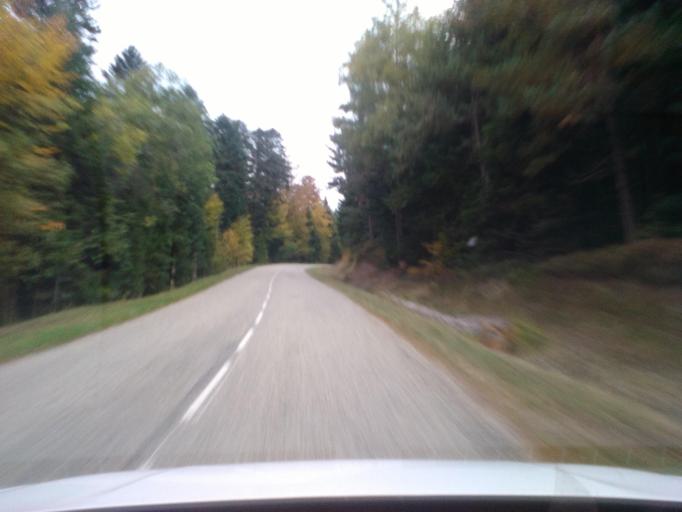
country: FR
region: Lorraine
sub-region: Departement des Vosges
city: Ban-de-Laveline
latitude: 48.3676
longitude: 7.1065
